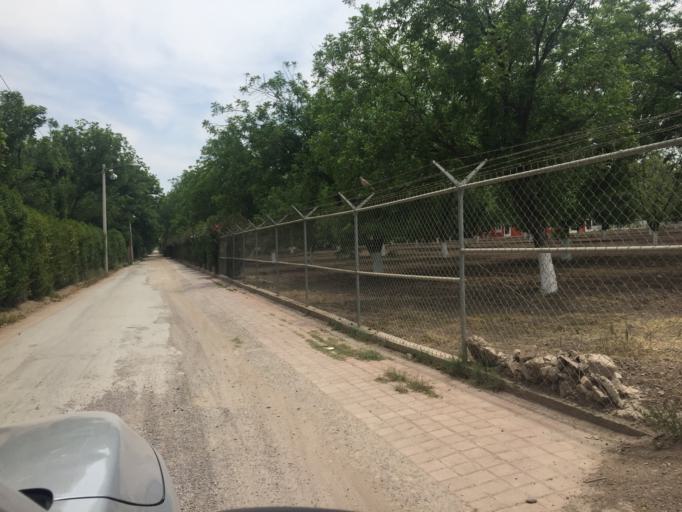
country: MX
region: Durango
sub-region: Gomez Palacio
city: San Jose de Vinedo
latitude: 25.6818
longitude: -103.4323
